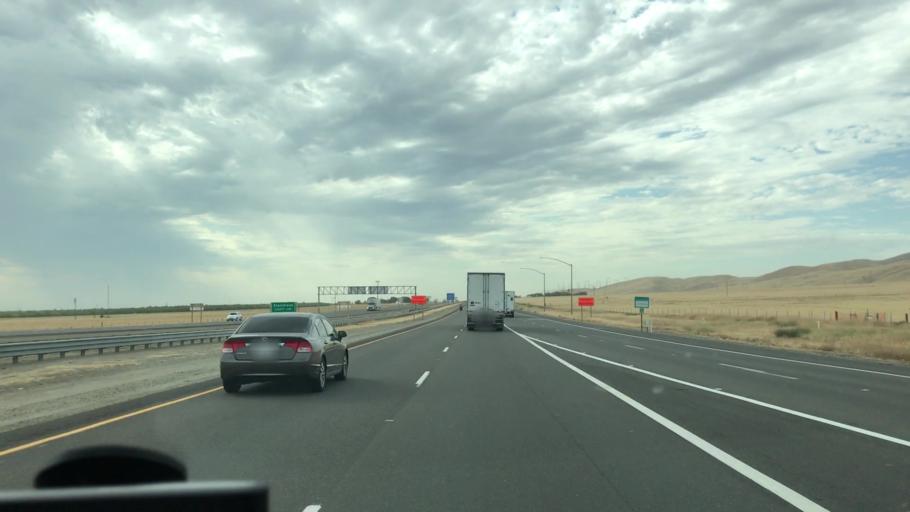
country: US
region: California
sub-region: San Joaquin County
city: Tracy
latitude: 37.5913
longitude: -121.3344
